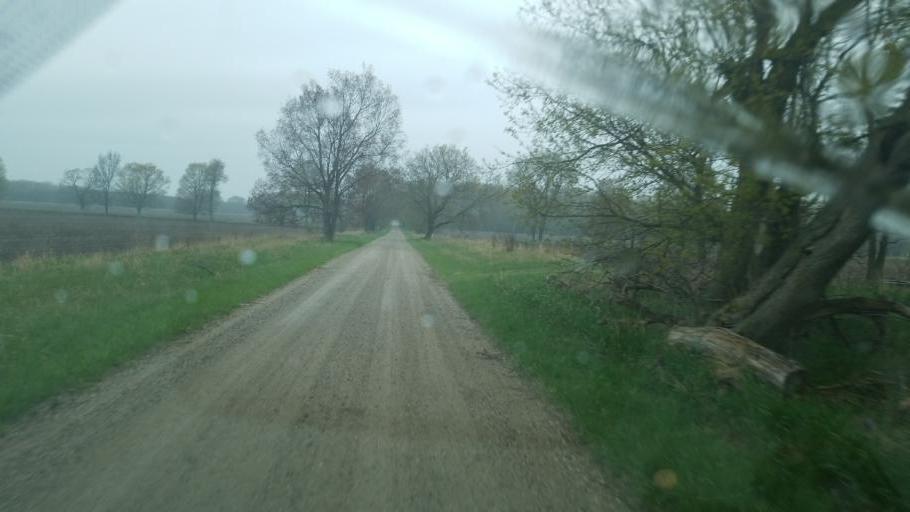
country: US
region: Michigan
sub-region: Mecosta County
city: Canadian Lakes
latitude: 43.5134
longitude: -85.3139
